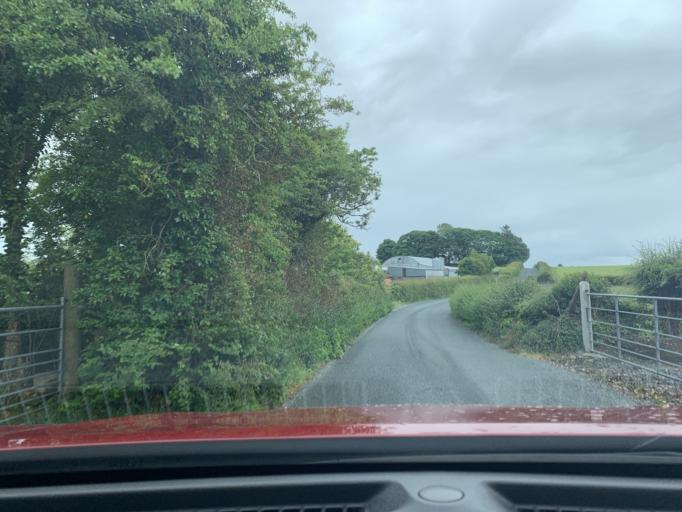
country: IE
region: Connaught
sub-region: Sligo
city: Sligo
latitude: 54.3110
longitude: -8.4752
